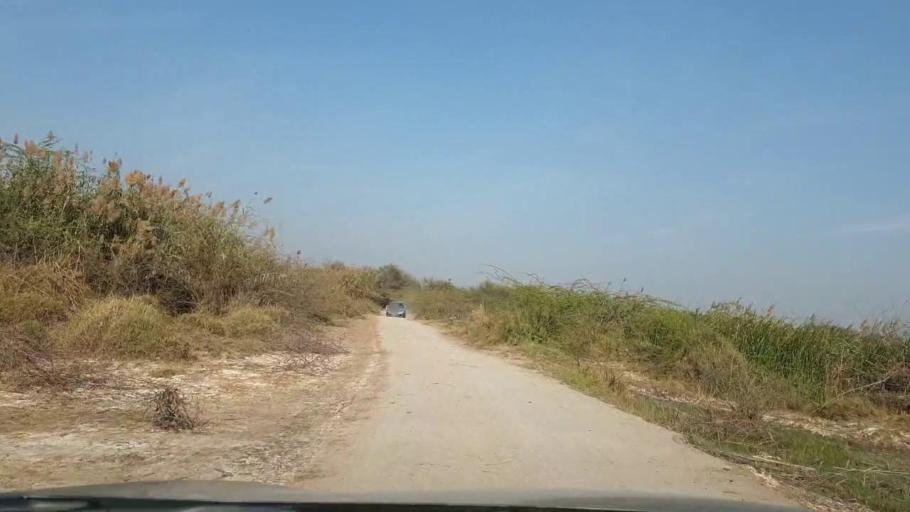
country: PK
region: Sindh
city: Berani
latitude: 25.6854
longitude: 68.7771
